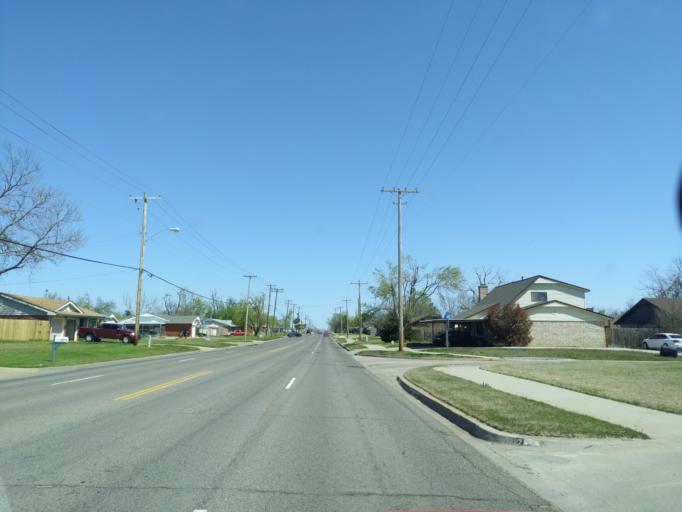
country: US
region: Oklahoma
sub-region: Cleveland County
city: Moore
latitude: 35.3488
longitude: -97.5106
